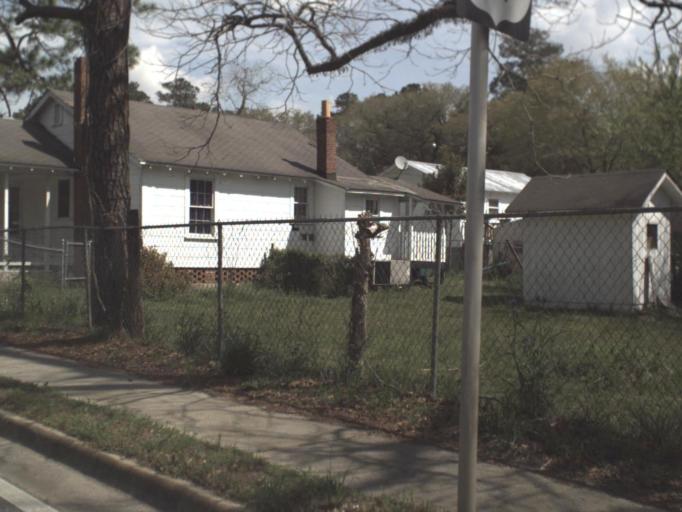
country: US
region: Florida
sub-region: Gadsden County
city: Havana
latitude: 30.6281
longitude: -84.4149
